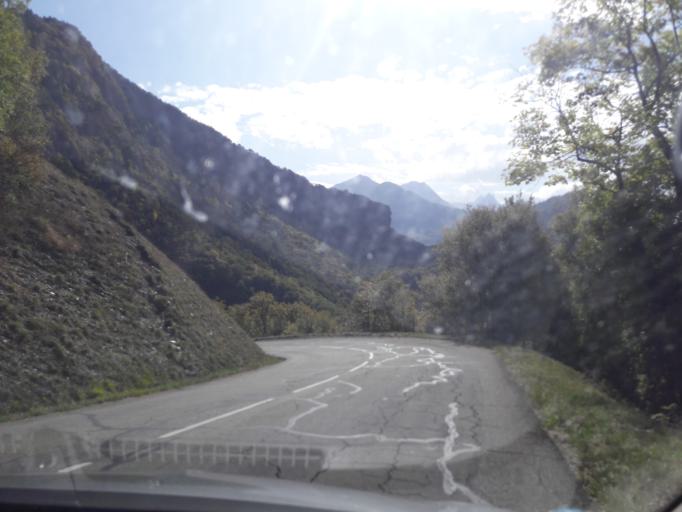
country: FR
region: Rhone-Alpes
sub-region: Departement de la Savoie
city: Saint-Jean-de-Maurienne
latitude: 45.3025
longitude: 6.3674
